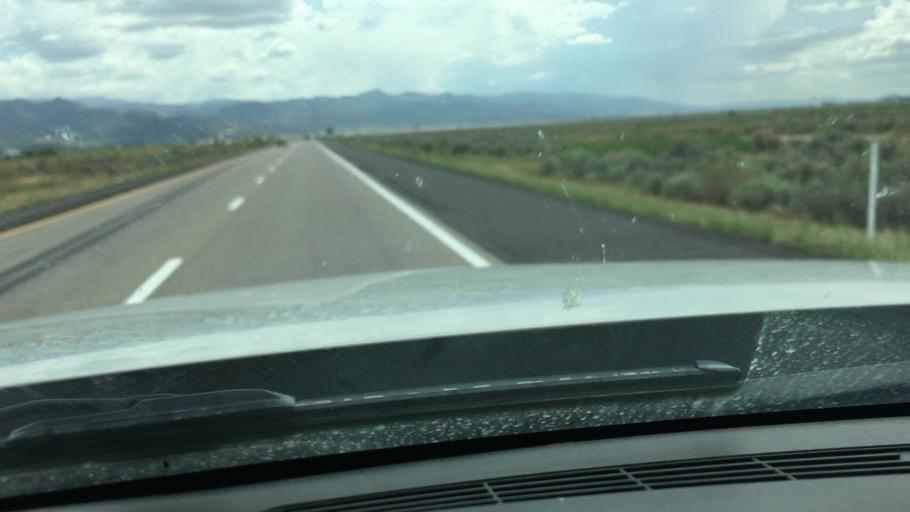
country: US
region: Utah
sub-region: Iron County
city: Parowan
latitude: 37.9294
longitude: -112.7658
